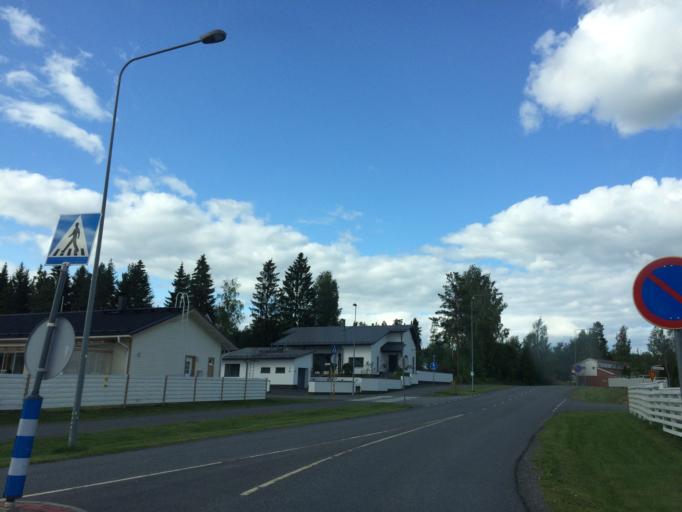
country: FI
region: Haeme
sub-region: Haemeenlinna
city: Parola
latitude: 60.9779
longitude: 24.3716
